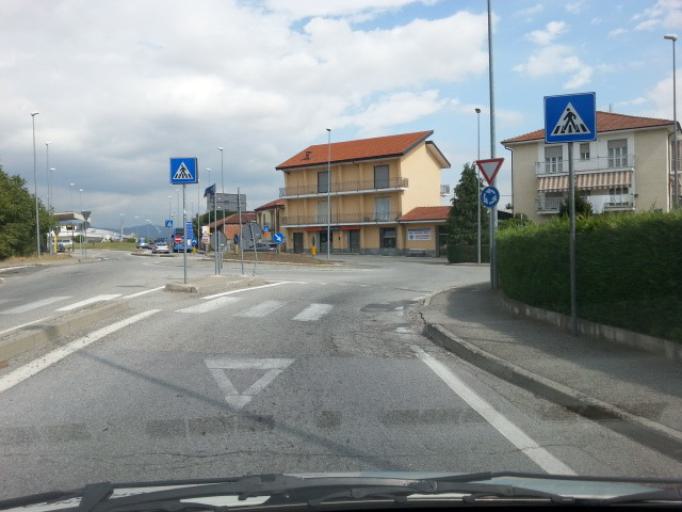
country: IT
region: Piedmont
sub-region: Provincia di Torino
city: Frossasco
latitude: 44.9243
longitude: 7.3673
